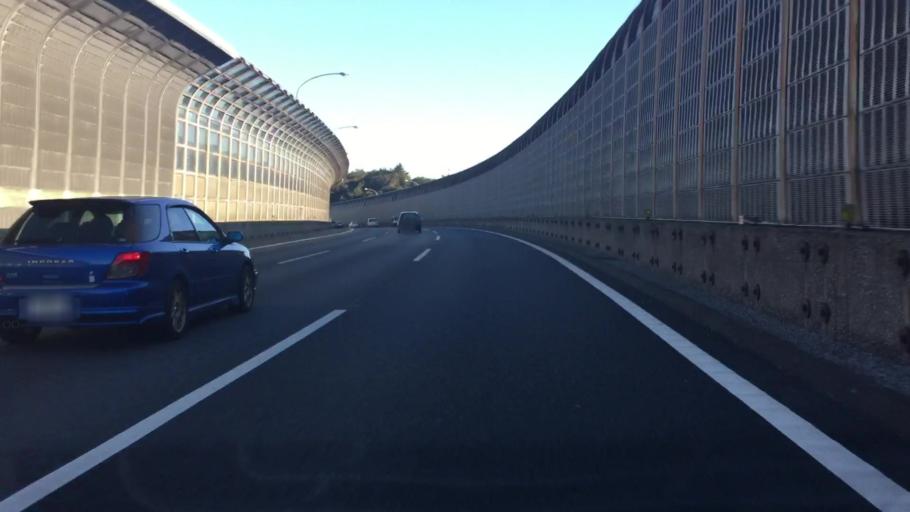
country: JP
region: Chiba
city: Chiba
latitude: 35.6418
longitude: 140.0720
